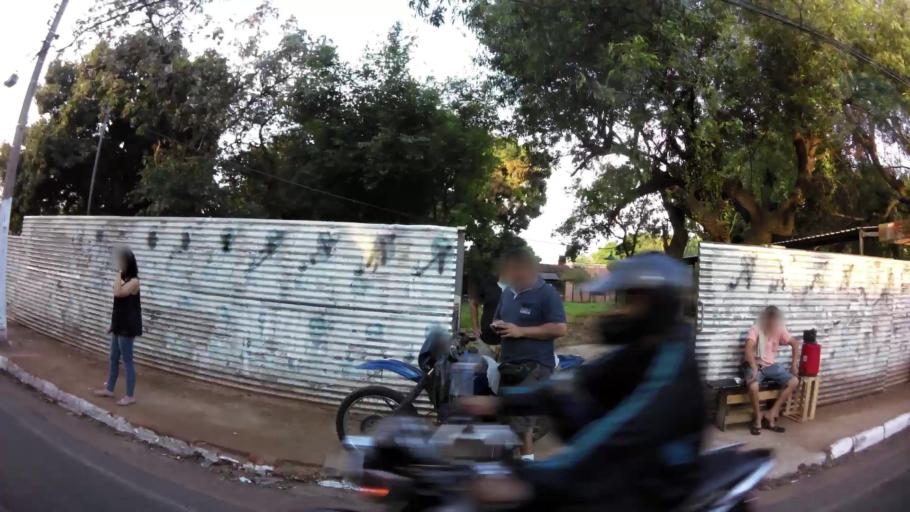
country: PY
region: Central
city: San Lorenzo
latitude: -25.3467
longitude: -57.5041
